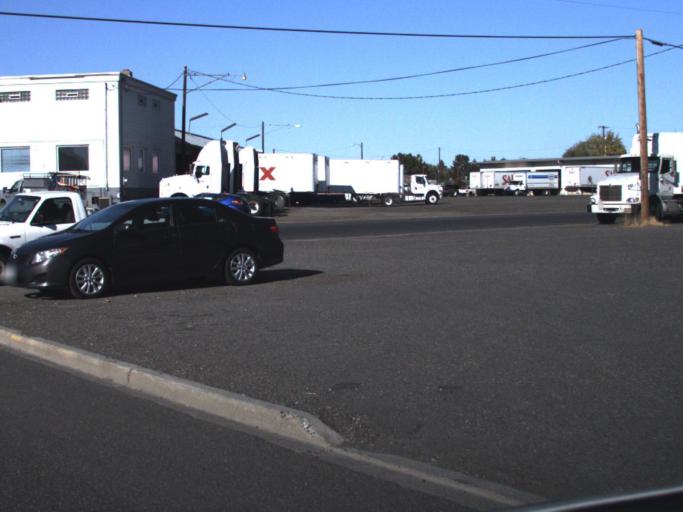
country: US
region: Washington
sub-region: Franklin County
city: Pasco
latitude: 46.2312
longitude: -119.0790
